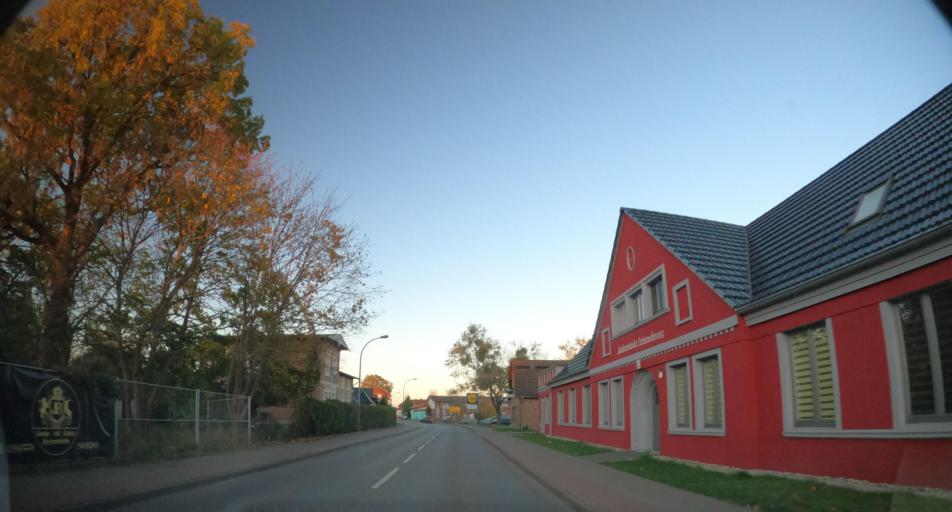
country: DE
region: Mecklenburg-Vorpommern
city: Ueckermunde
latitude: 53.7373
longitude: 14.0403
